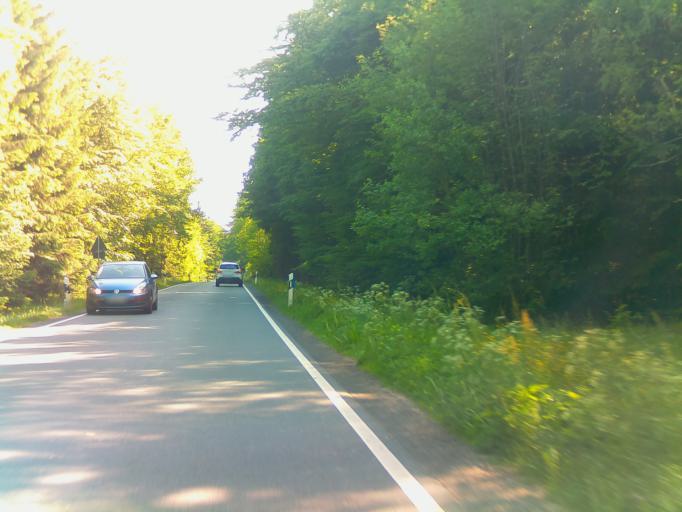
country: DE
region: Hesse
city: Michelstadt
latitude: 49.6876
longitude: 9.0836
